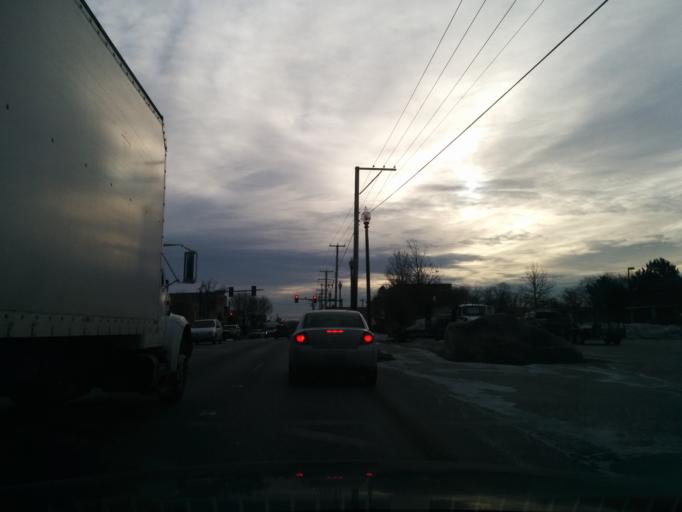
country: US
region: Illinois
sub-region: Cook County
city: Schiller Park
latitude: 41.9546
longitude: -87.8650
